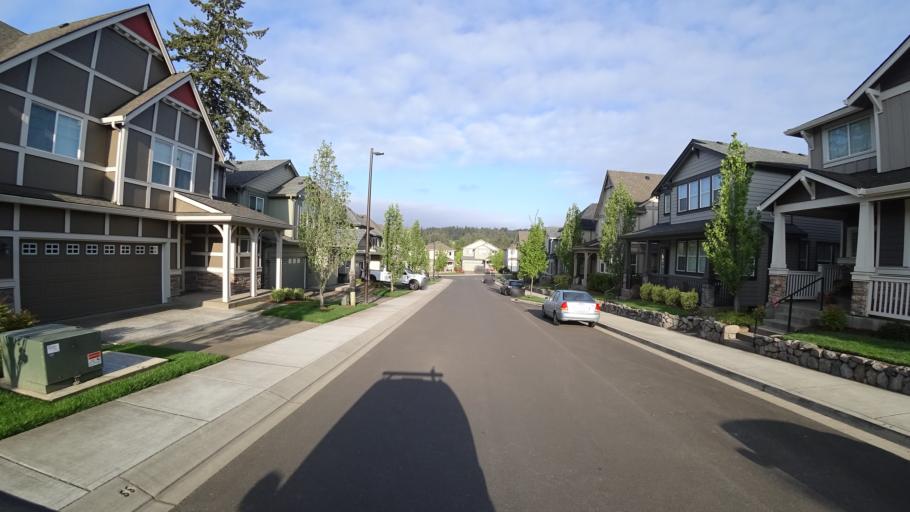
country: US
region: Oregon
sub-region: Washington County
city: Beaverton
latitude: 45.4461
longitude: -122.8243
